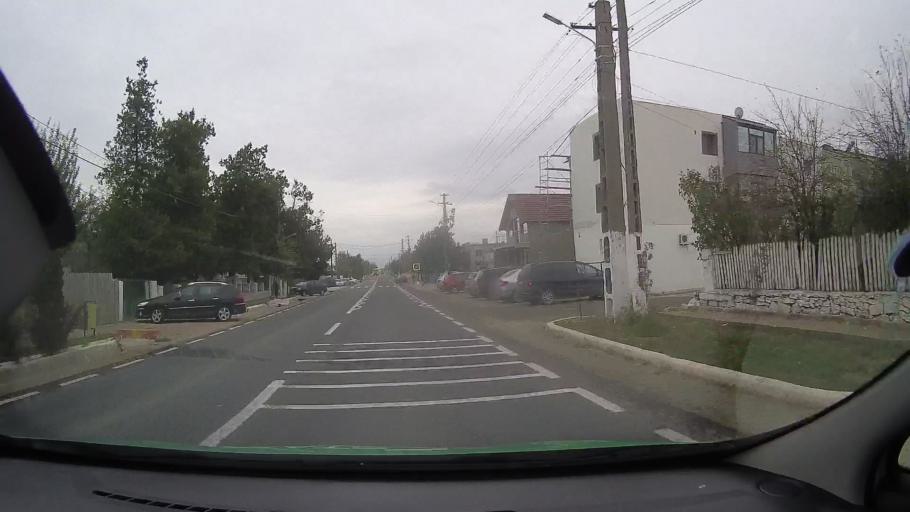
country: RO
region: Constanta
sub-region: Comuna Nicolae Balcescu
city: Nicolae Balcescu
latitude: 44.3885
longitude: 28.3768
